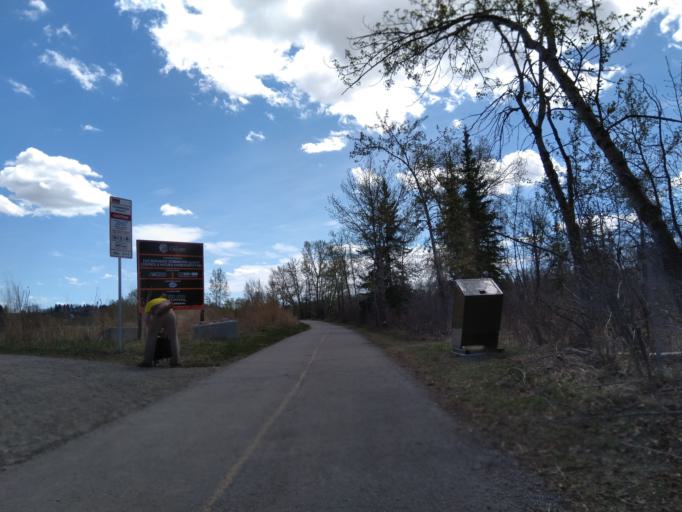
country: CA
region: Alberta
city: Calgary
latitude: 51.0895
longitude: -114.1798
